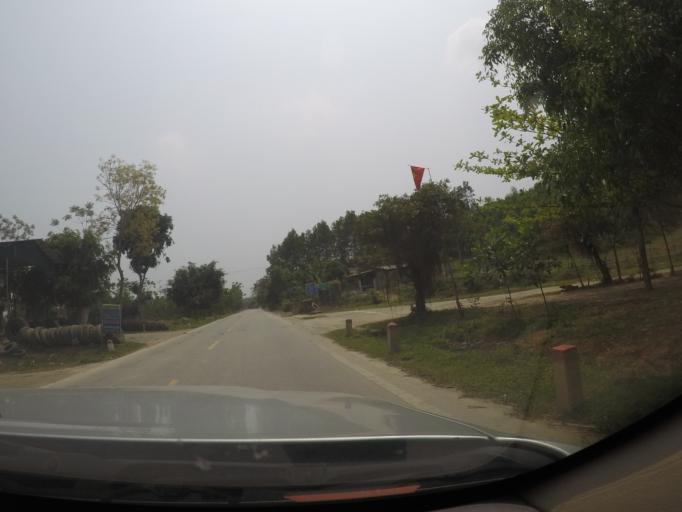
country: VN
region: Thanh Hoa
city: Thi Tran Yen Cat
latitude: 19.7443
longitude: 105.4235
